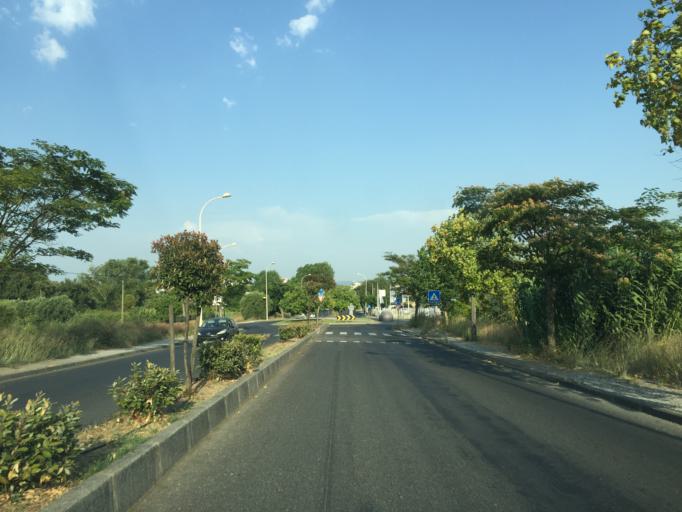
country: PT
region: Santarem
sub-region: Torres Novas
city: Torres Novas
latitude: 39.4739
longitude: -8.5538
